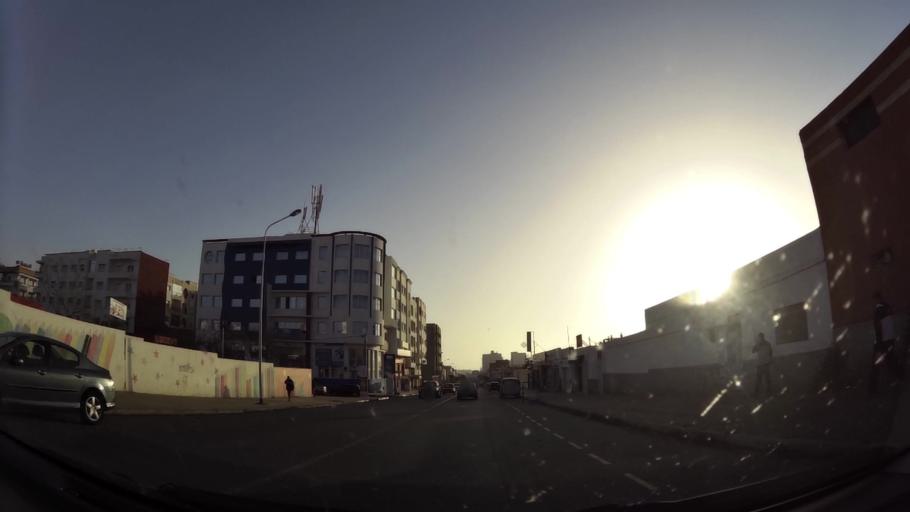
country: MA
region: Oued ed Dahab-Lagouira
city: Dakhla
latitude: 30.4164
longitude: -9.5751
